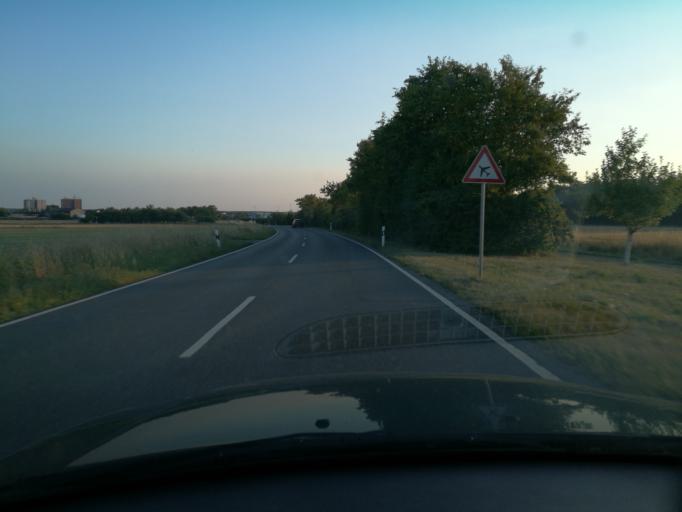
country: DE
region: Bavaria
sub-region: Regierungsbezirk Mittelfranken
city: Herzogenaurach
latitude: 49.5853
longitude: 10.8875
